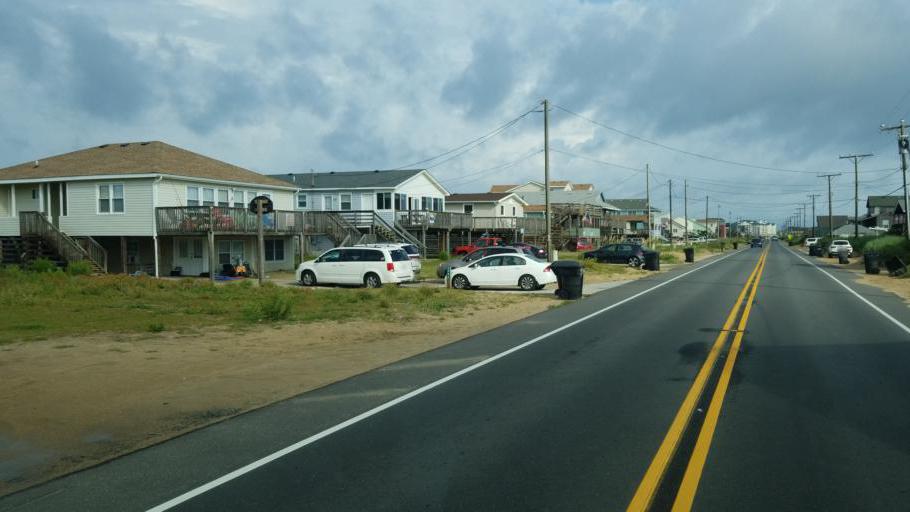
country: US
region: North Carolina
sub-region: Dare County
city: Kitty Hawk
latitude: 36.0919
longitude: -75.7061
